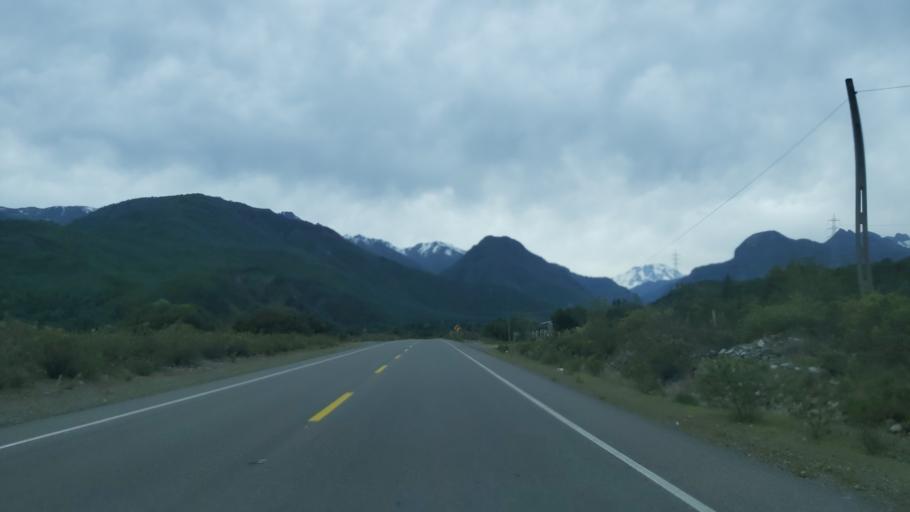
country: CL
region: Maule
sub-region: Provincia de Linares
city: Colbun
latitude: -35.7121
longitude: -71.1112
